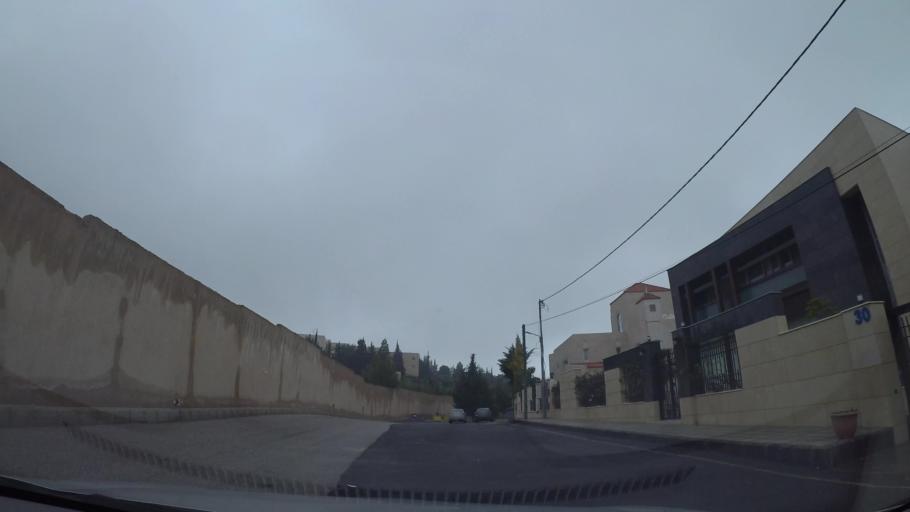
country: JO
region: Amman
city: Al Jubayhah
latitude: 32.0084
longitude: 35.8219
